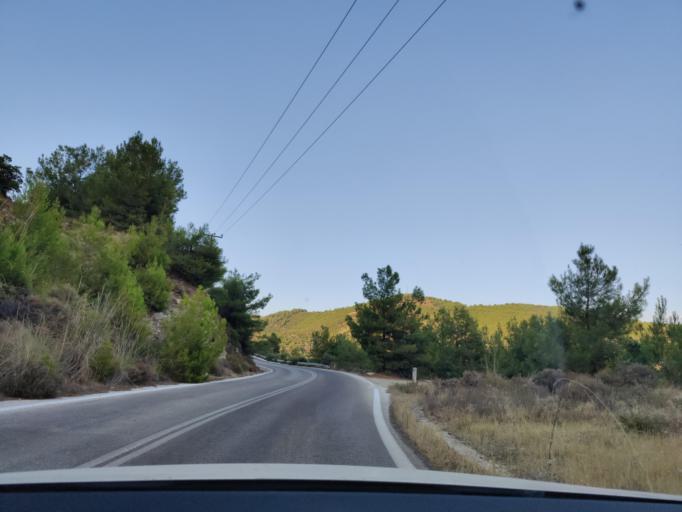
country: GR
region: East Macedonia and Thrace
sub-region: Nomos Kavalas
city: Potamia
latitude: 40.6161
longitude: 24.7558
